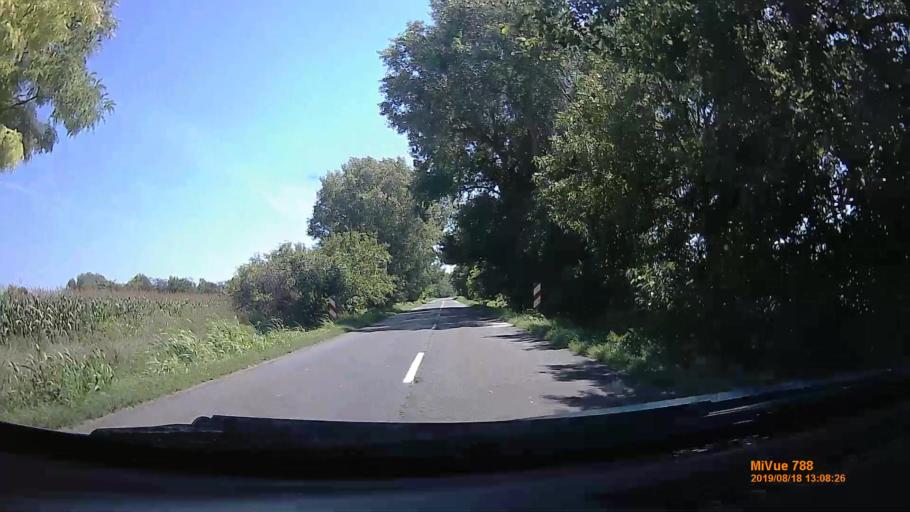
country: HU
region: Fejer
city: Kaloz
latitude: 46.9389
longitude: 18.5025
